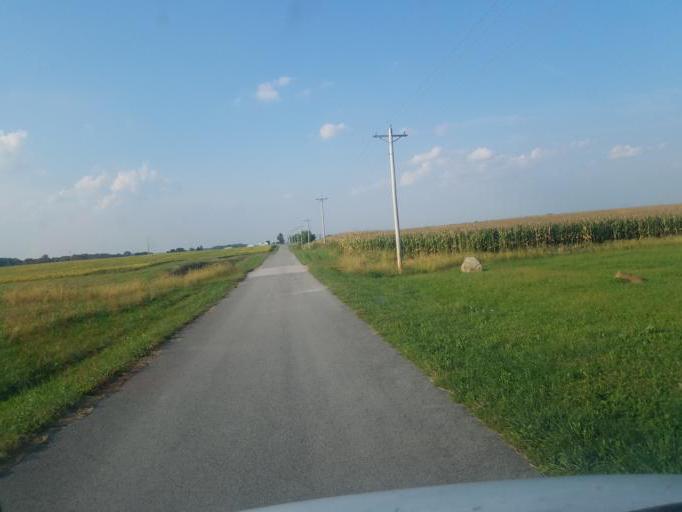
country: US
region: Ohio
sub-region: Seneca County
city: Tiffin
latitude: 40.9600
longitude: -83.1124
